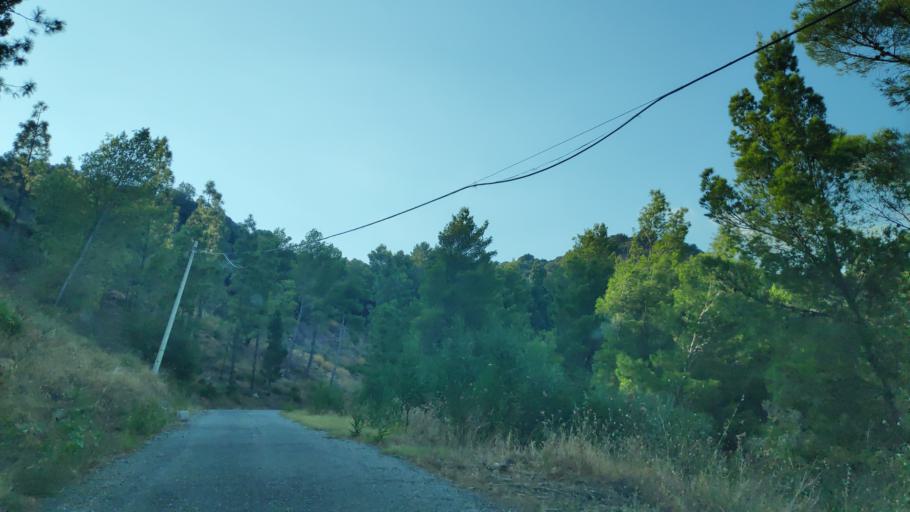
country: IT
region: Calabria
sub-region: Provincia di Reggio Calabria
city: Placanica
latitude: 38.4104
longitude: 16.4308
